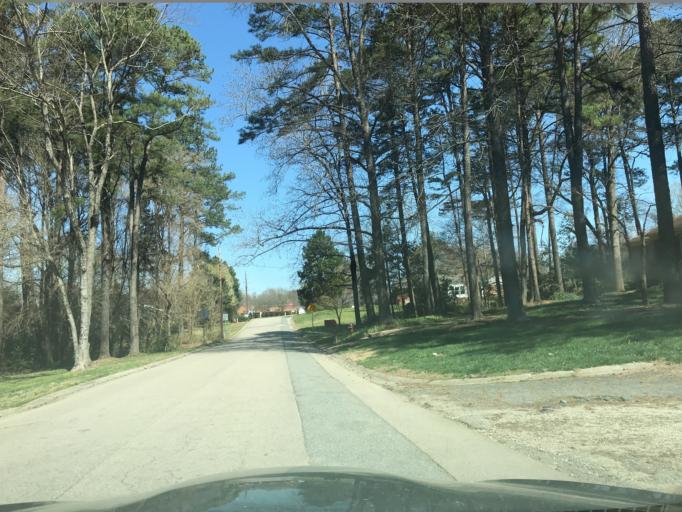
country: US
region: North Carolina
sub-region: Wake County
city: Raleigh
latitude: 35.8469
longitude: -78.5976
